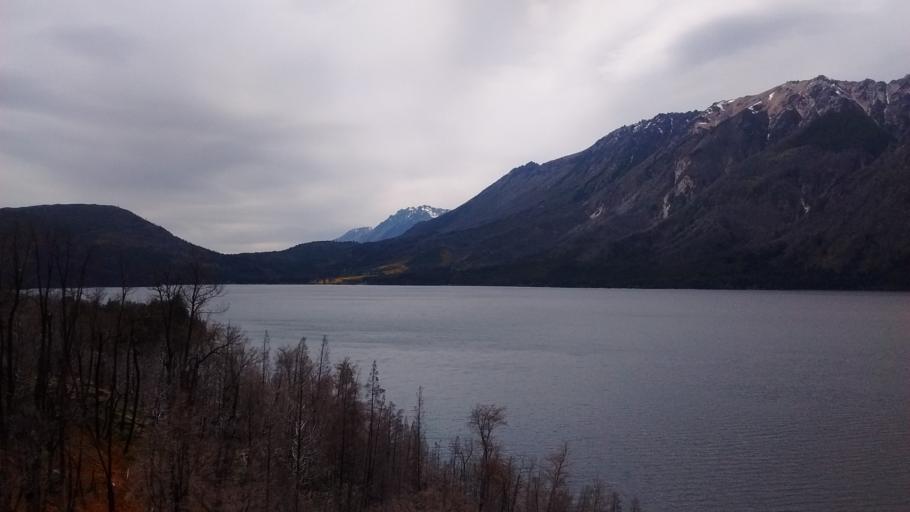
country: AR
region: Chubut
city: Hoyo de Epuyen
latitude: -42.1831
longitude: -71.5398
